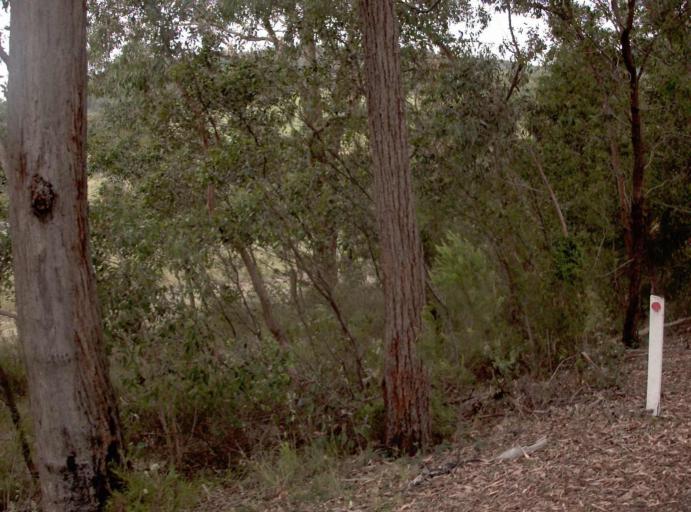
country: AU
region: Victoria
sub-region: East Gippsland
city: Bairnsdale
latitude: -37.7320
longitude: 147.5919
